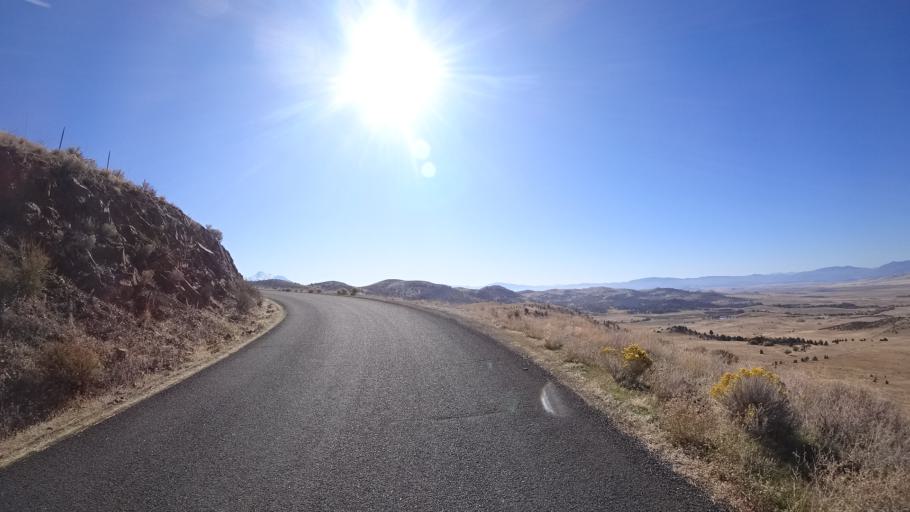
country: US
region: California
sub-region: Siskiyou County
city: Montague
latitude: 41.8258
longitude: -122.3447
